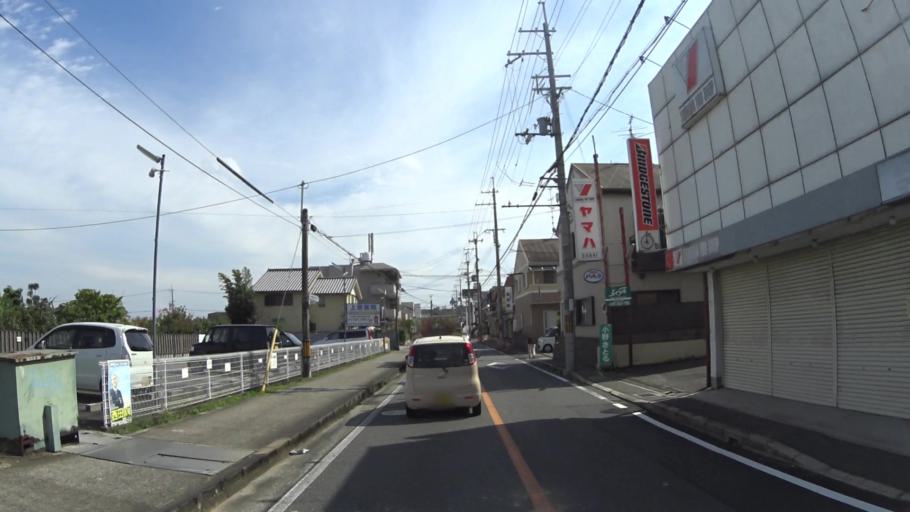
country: JP
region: Kyoto
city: Muko
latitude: 34.9685
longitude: 135.6941
